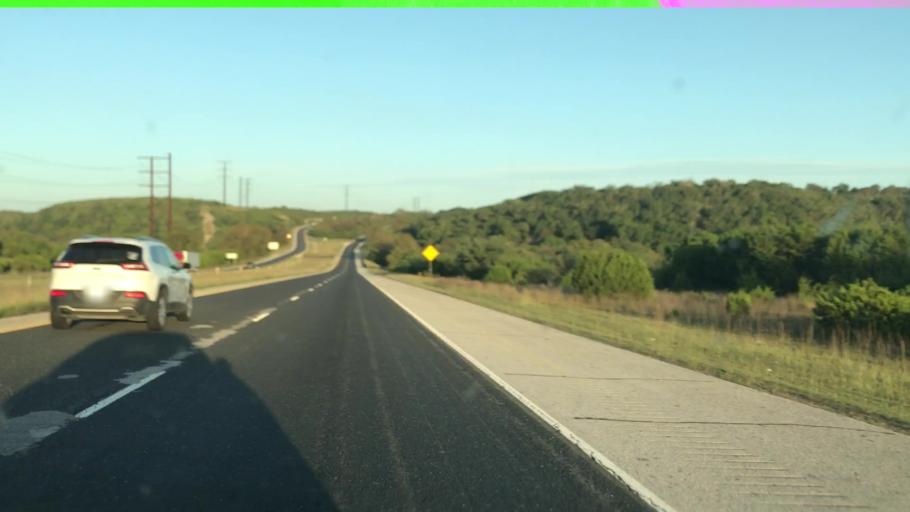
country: US
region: Texas
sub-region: Kerr County
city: Kerrville
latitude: 30.0694
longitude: -99.0915
